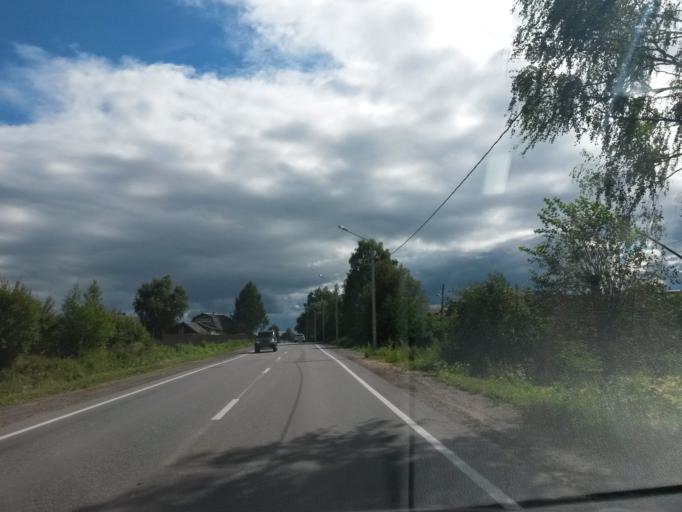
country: RU
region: Jaroslavl
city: Gavrilov-Yam
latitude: 57.3536
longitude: 39.9083
